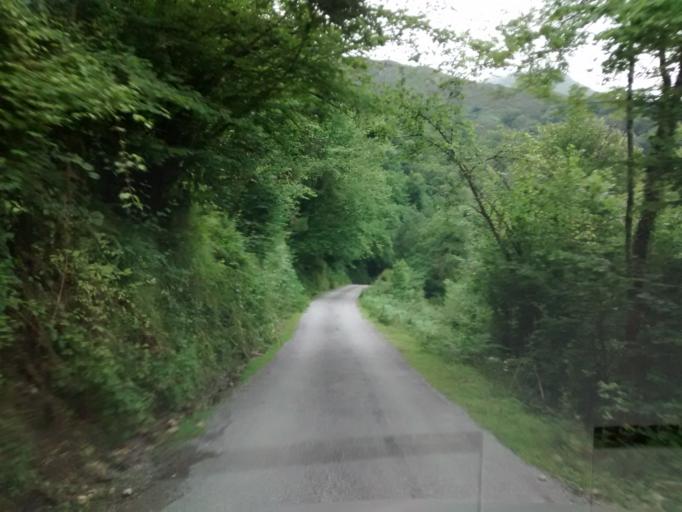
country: ES
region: Asturias
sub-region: Province of Asturias
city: Pilona
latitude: 43.2725
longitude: -5.3456
